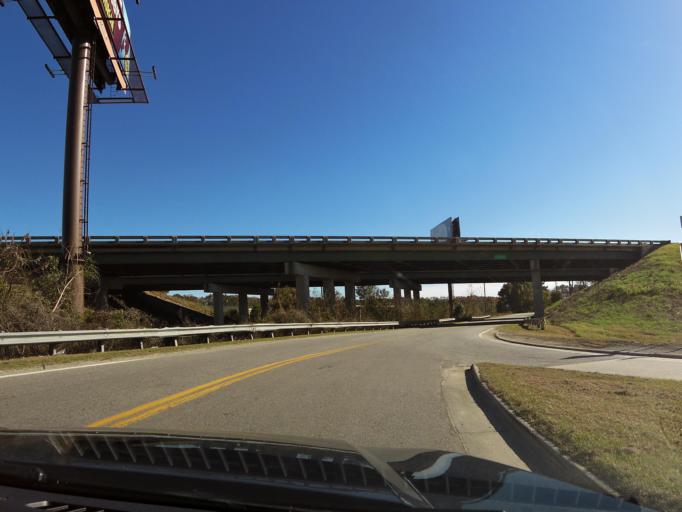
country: US
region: Georgia
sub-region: Chatham County
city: Savannah
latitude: 32.0670
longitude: -81.1375
